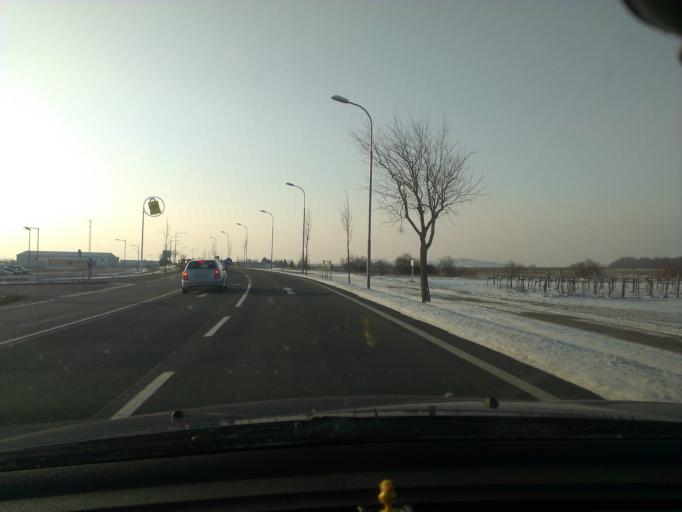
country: AT
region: Burgenland
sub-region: Eisenstadt-Umgebung
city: Donnerskirchen
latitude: 47.8788
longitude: 16.6480
